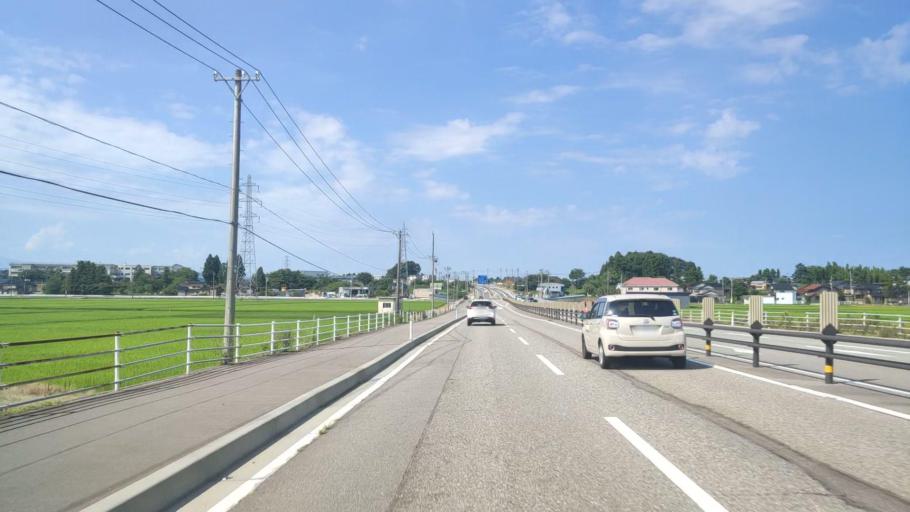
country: JP
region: Ishikawa
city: Komatsu
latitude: 36.4148
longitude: 136.5129
